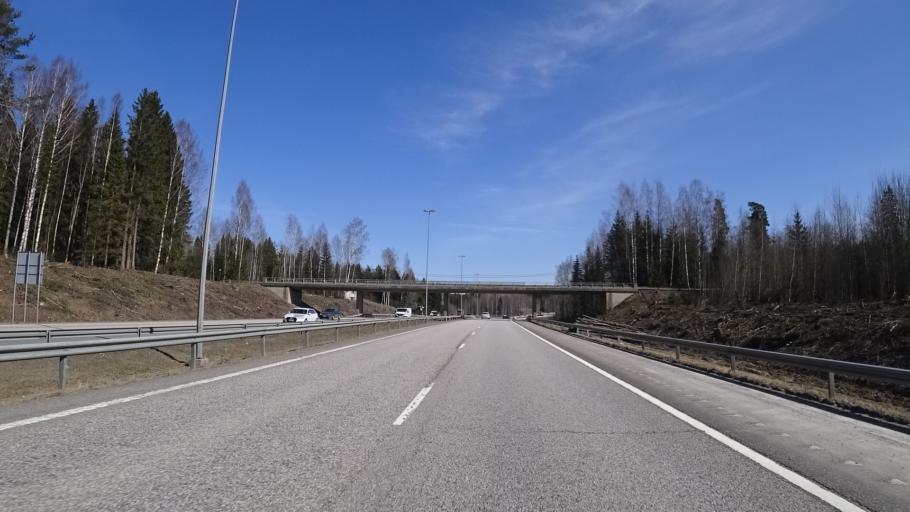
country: FI
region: Uusimaa
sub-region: Helsinki
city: Vihti
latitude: 60.2934
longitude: 24.3439
